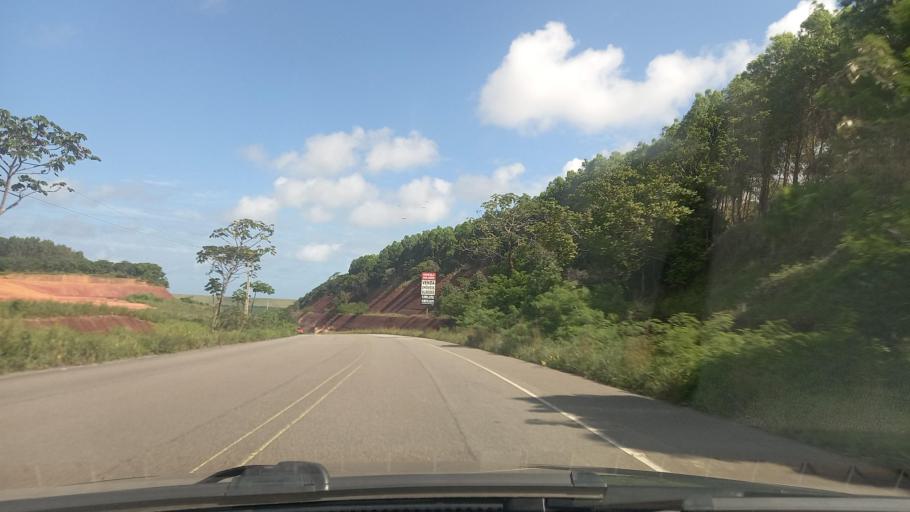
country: BR
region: Alagoas
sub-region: Marechal Deodoro
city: Marechal Deodoro
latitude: -9.8295
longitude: -35.9292
